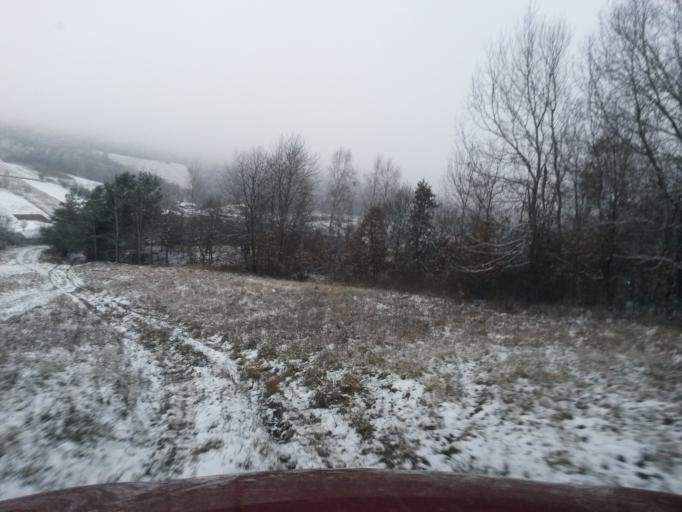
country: SK
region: Presovsky
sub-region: Okres Presov
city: Presov
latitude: 48.9771
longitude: 21.1176
